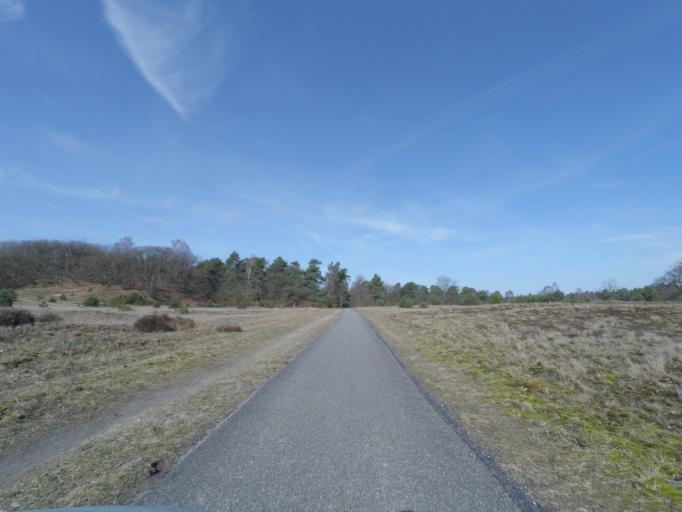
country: NL
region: Gelderland
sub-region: Gemeente Barneveld
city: Garderen
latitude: 52.2031
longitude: 5.7636
